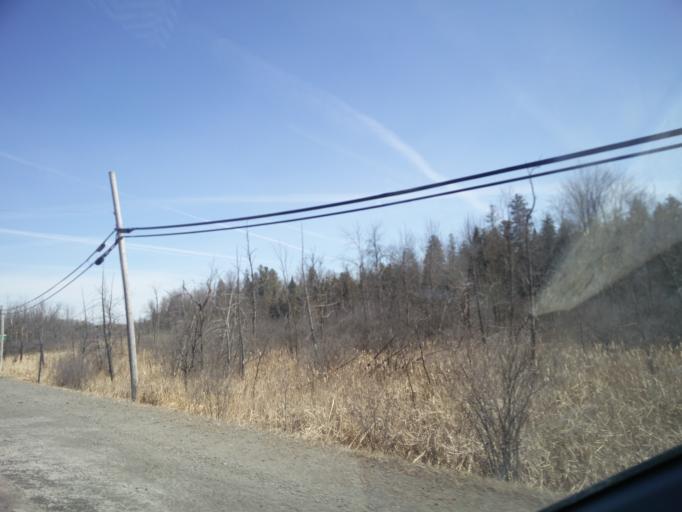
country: CA
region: Ontario
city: Bells Corners
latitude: 45.1748
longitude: -75.6399
